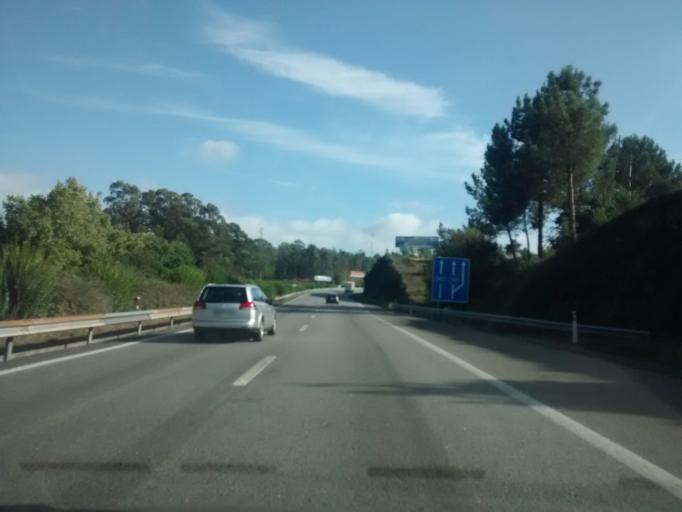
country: PT
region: Porto
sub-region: Santo Tirso
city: Santo Tirso
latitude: 41.3491
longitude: -8.5069
